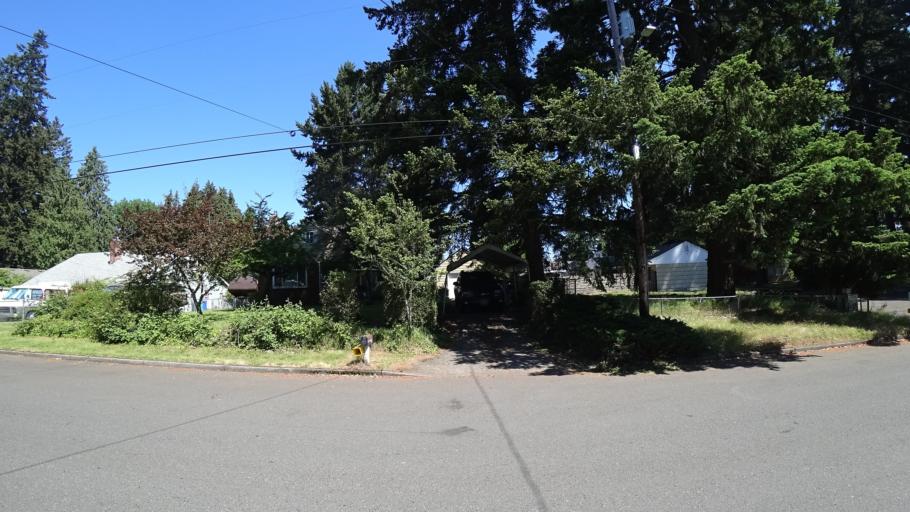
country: US
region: Oregon
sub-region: Clackamas County
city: Happy Valley
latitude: 45.4748
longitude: -122.5310
